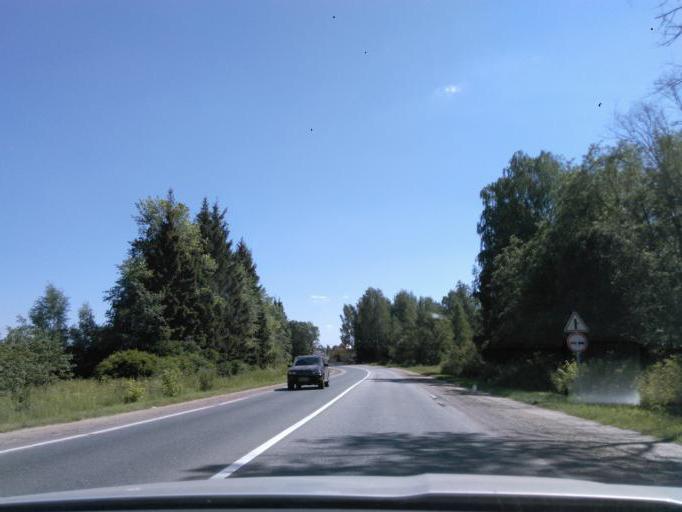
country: RU
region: Moskovskaya
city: Solnechnogorsk
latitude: 56.1409
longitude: 36.9169
